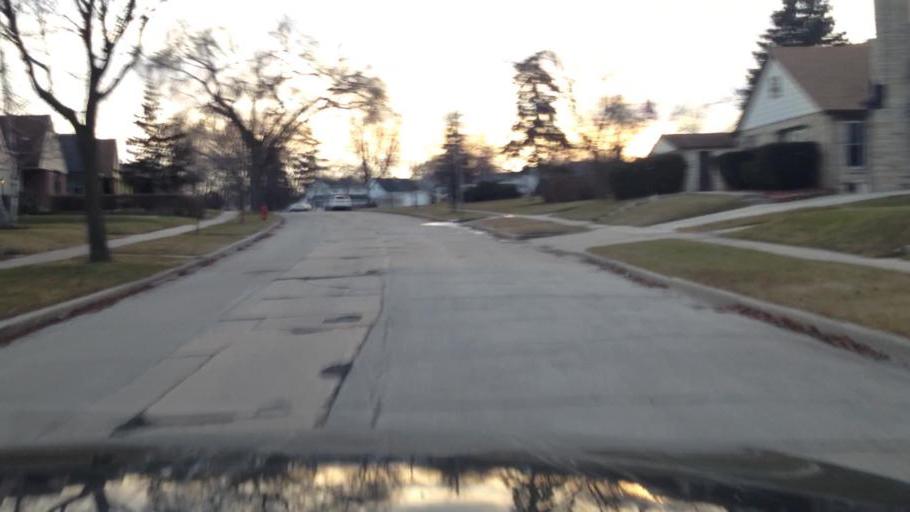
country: US
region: Wisconsin
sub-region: Milwaukee County
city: West Milwaukee
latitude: 42.9972
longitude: -87.9903
